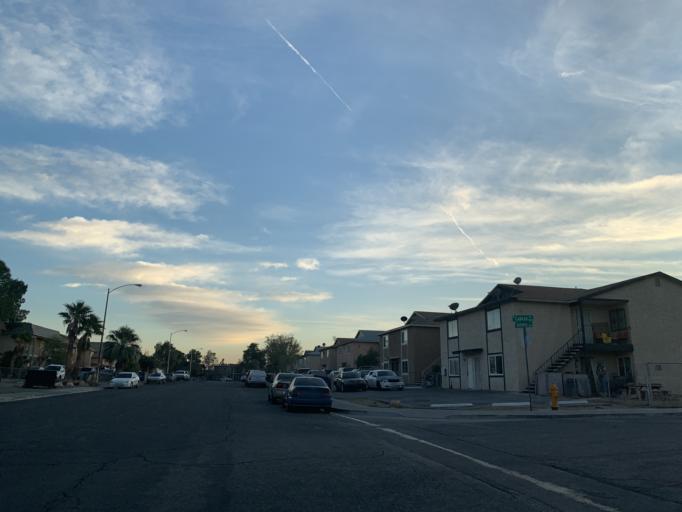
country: US
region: Nevada
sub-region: Clark County
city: Spring Valley
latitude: 36.1144
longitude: -115.2150
